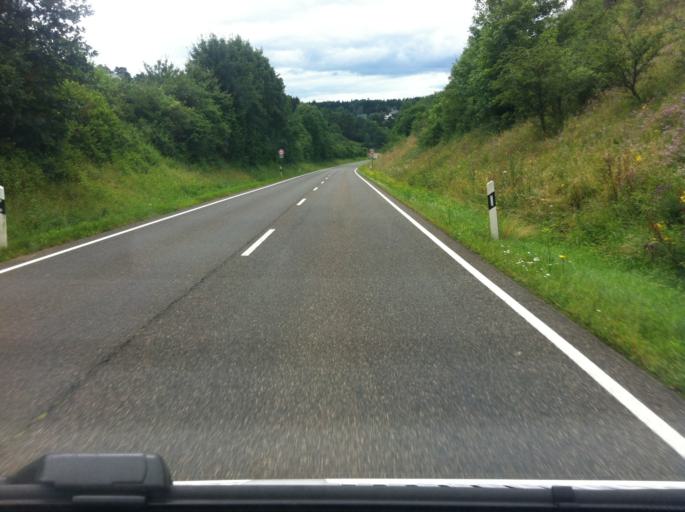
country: DE
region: North Rhine-Westphalia
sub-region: Regierungsbezirk Koln
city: Nettersheim
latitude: 50.5003
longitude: 6.6330
